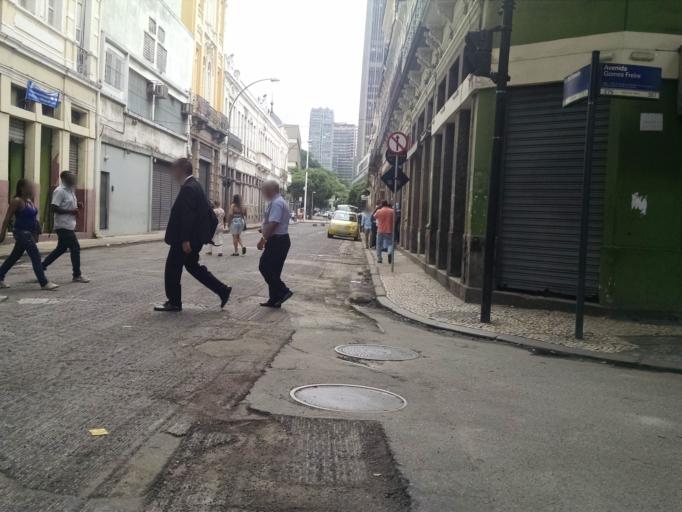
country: BR
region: Rio de Janeiro
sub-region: Rio De Janeiro
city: Rio de Janeiro
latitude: -22.9095
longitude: -43.1845
